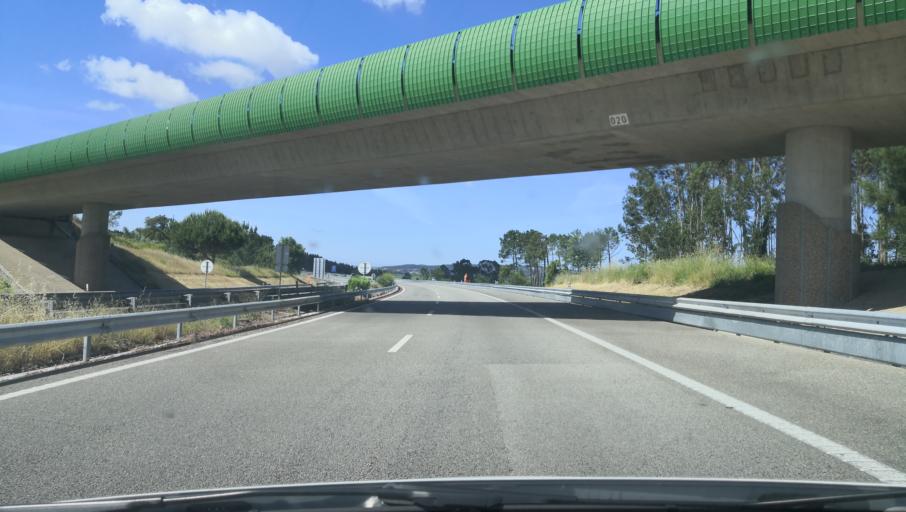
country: PT
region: Coimbra
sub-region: Montemor-O-Velho
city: Montemor-o-Velho
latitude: 40.1904
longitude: -8.6976
